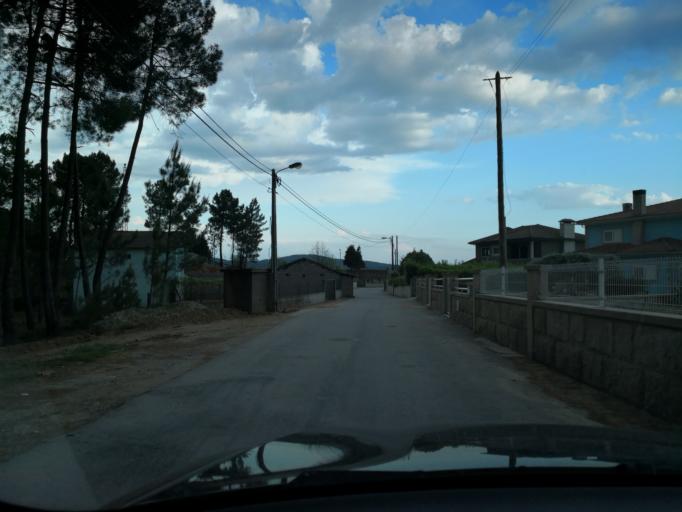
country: PT
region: Vila Real
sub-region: Vila Real
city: Vila Real
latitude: 41.2696
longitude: -7.6894
